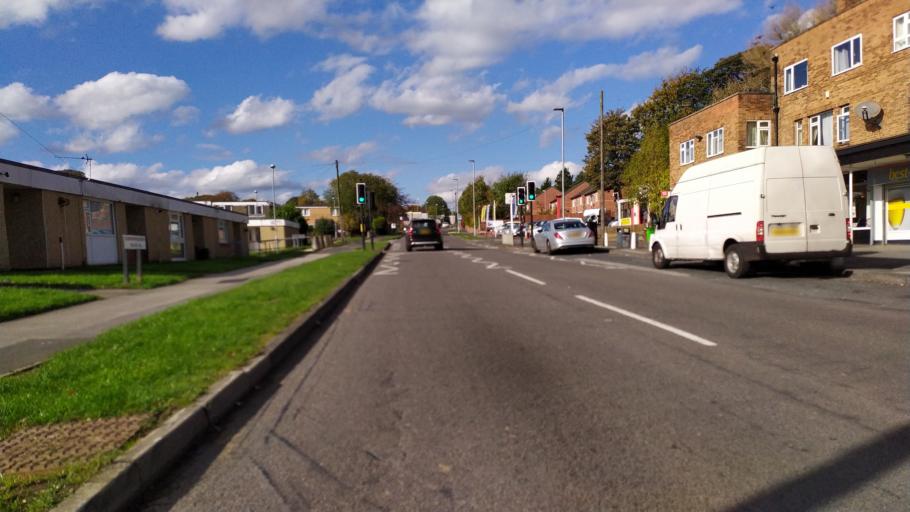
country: GB
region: England
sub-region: City and Borough of Leeds
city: Horsforth
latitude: 53.8215
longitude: -1.5969
